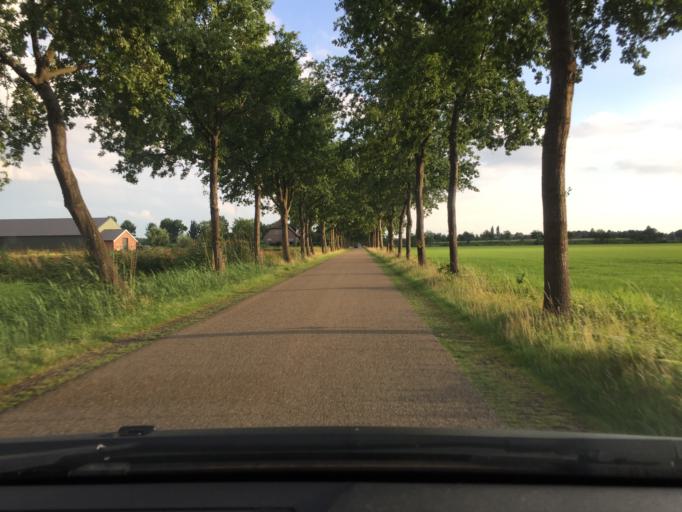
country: NL
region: North Brabant
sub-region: Gemeente Veghel
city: Keldonk
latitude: 51.5831
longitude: 5.5686
